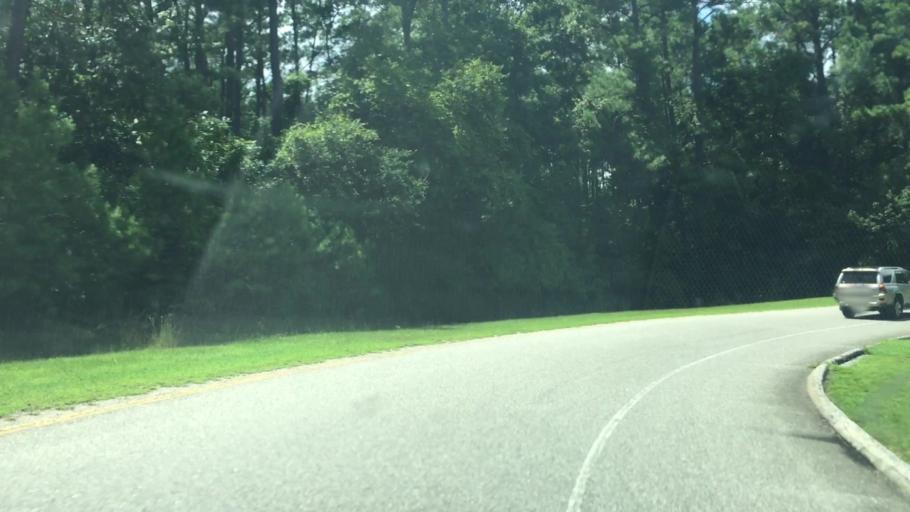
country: US
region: South Carolina
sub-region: Horry County
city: North Myrtle Beach
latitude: 33.8469
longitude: -78.6538
